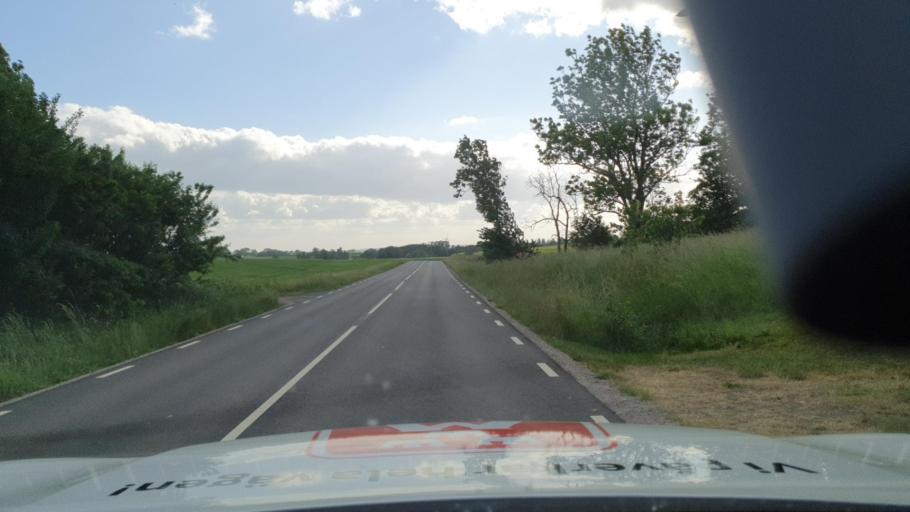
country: SE
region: Skane
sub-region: Tomelilla Kommun
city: Tomelilla
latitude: 55.5886
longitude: 14.0269
